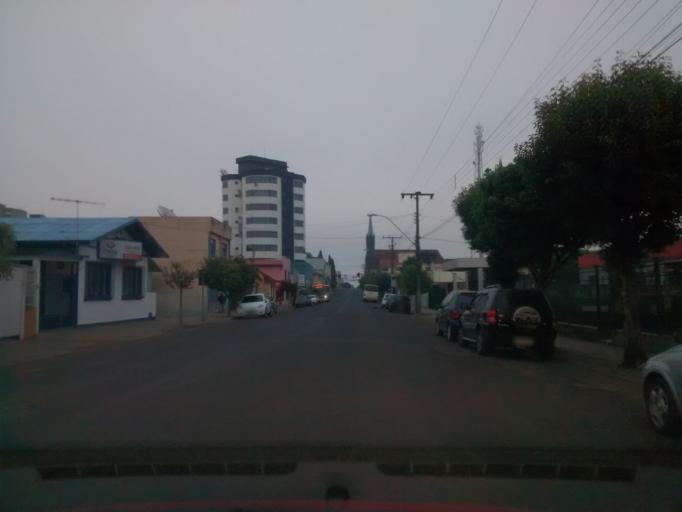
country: BR
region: Rio Grande do Sul
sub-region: Vacaria
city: Vacaria
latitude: -28.5026
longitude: -50.9338
